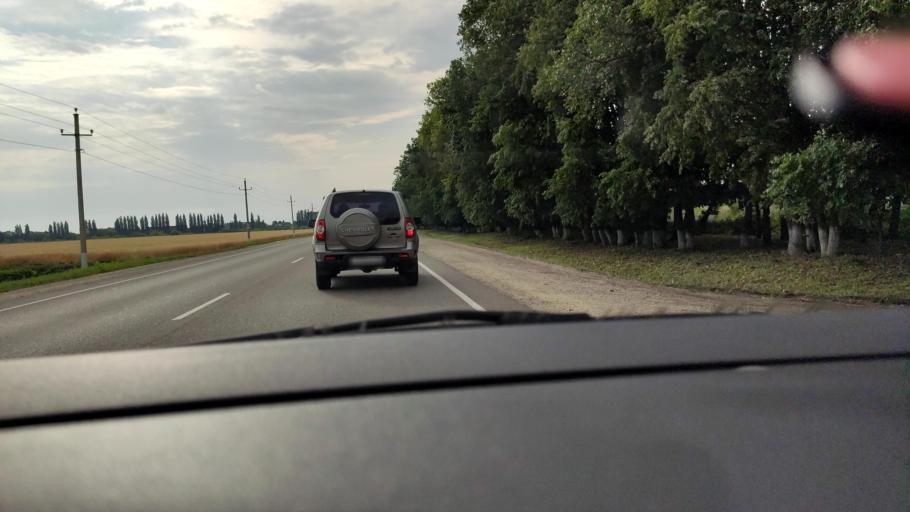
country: RU
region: Voronezj
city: Ramon'
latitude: 51.9220
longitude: 39.2818
